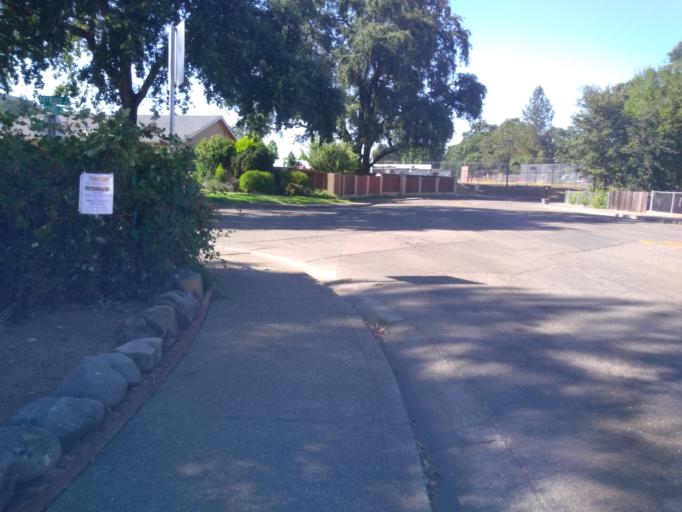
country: US
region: California
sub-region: Mendocino County
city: Ukiah
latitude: 39.1313
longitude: -123.2117
